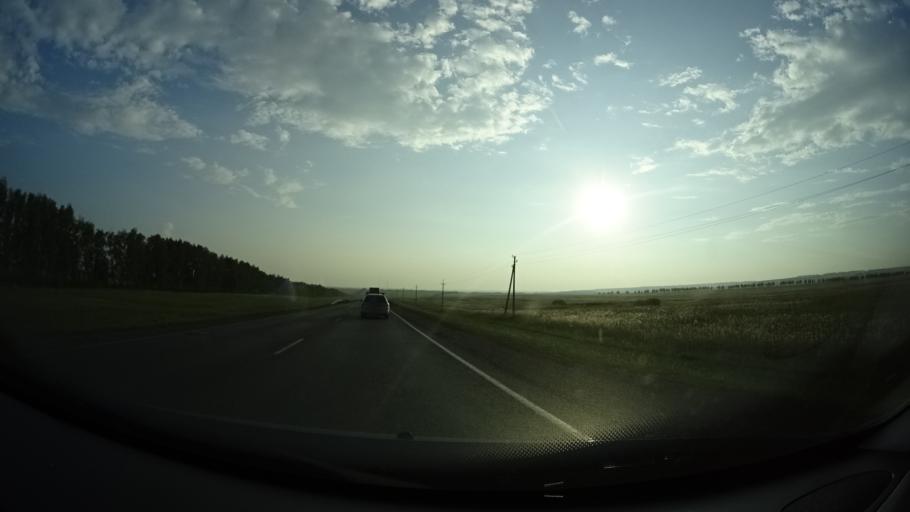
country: RU
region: Samara
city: Kamyshla
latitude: 54.0528
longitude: 52.0500
